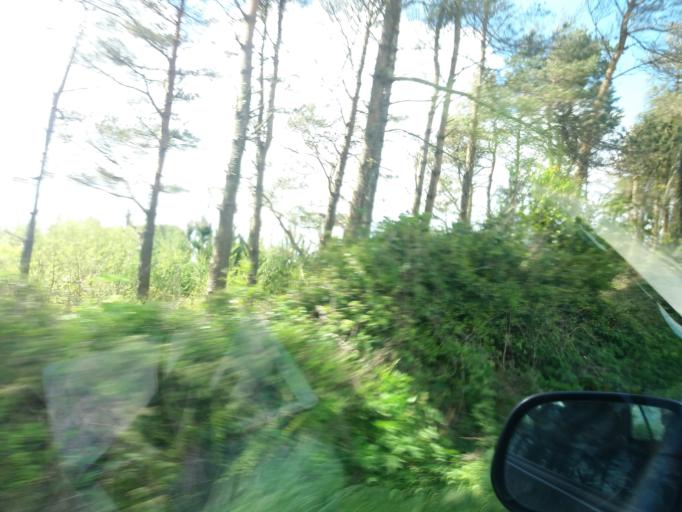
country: IE
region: Munster
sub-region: Waterford
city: Dunmore East
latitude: 52.2381
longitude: -6.9335
